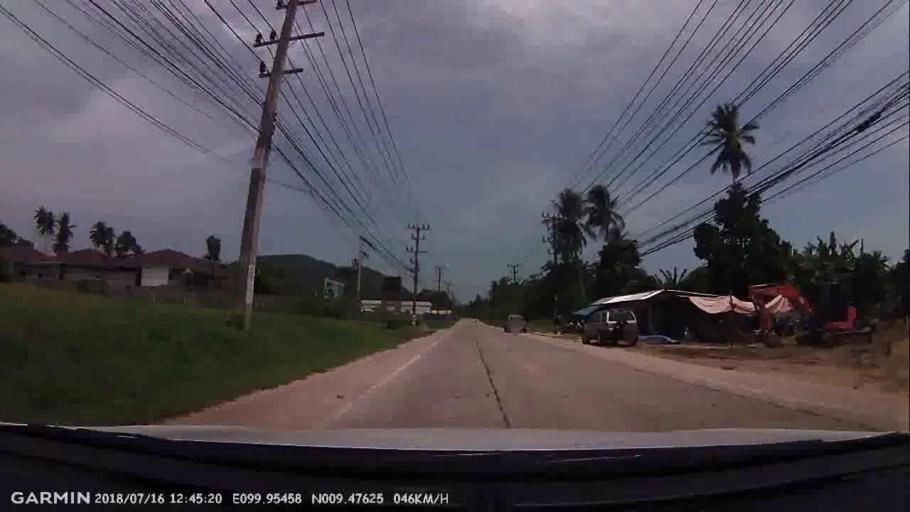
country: TH
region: Surat Thani
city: Ko Samui
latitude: 9.4761
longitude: 99.9545
